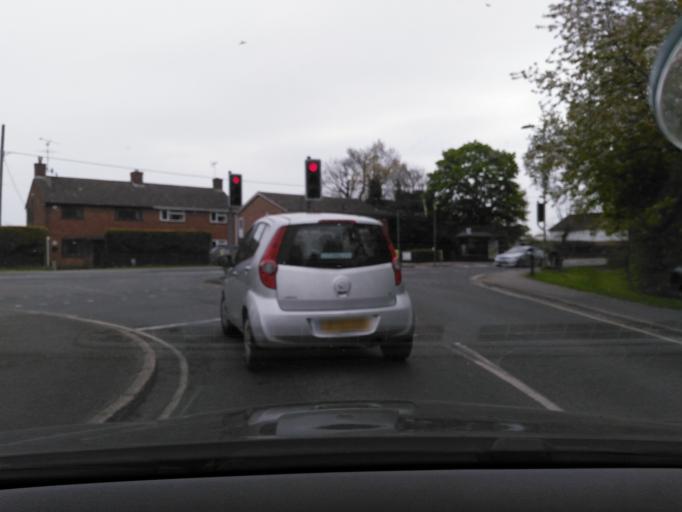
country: GB
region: England
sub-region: Hampshire
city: Tadley
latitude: 51.3567
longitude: -1.1438
